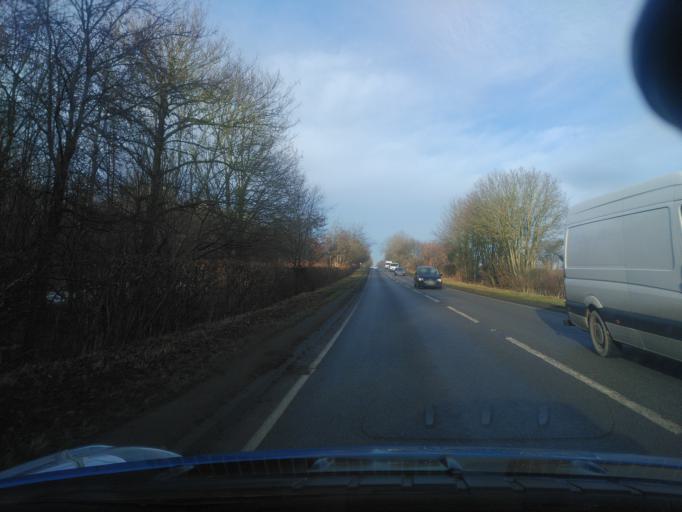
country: GB
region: England
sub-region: Oxfordshire
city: Woodstock
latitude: 51.8583
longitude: -1.3628
